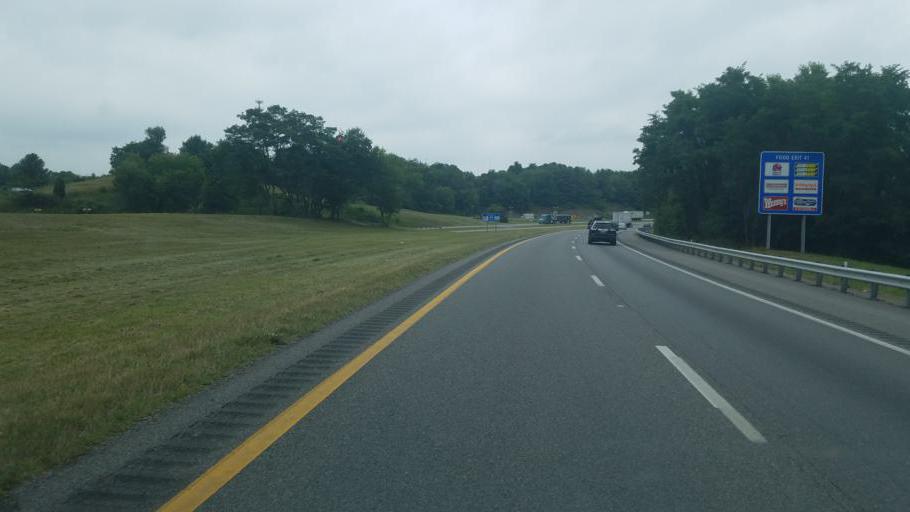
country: US
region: Virginia
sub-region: Wythe County
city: Wytheville
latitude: 36.9613
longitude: -81.0630
